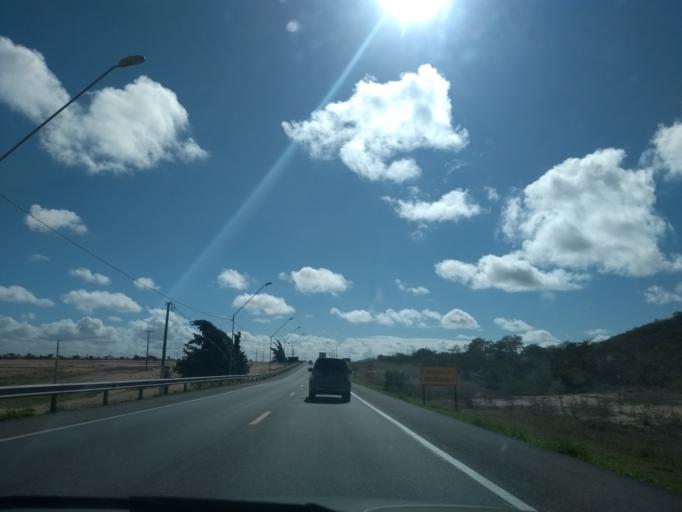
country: BR
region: Bahia
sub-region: Amargosa
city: Amargosa
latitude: -12.8627
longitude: -39.8525
